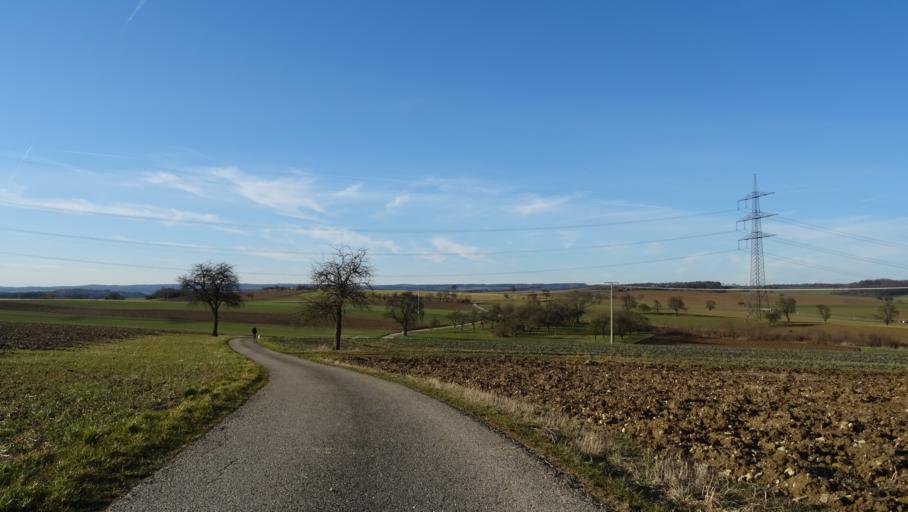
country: DE
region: Baden-Wuerttemberg
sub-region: Karlsruhe Region
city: Billigheim
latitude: 49.4126
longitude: 9.2702
